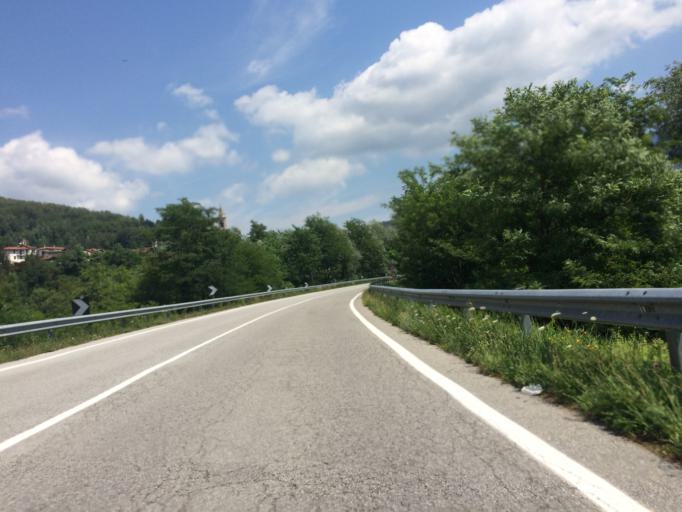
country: IT
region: Piedmont
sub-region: Provincia di Cuneo
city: Priola
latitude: 44.2380
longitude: 8.0156
